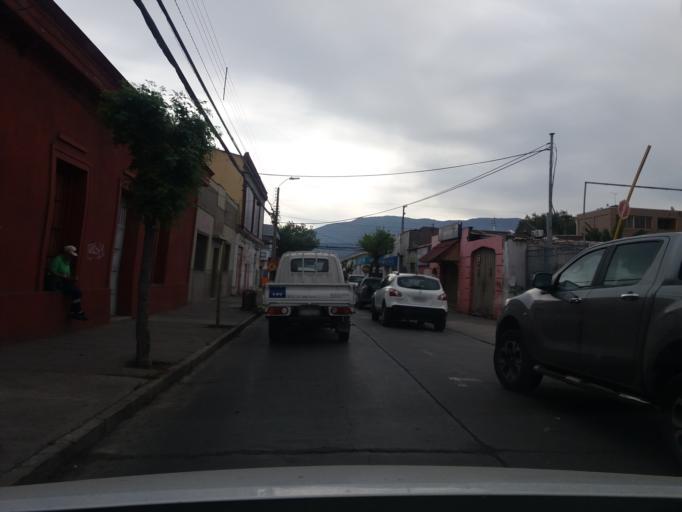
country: CL
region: Valparaiso
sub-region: Provincia de San Felipe
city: San Felipe
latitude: -32.7524
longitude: -70.7257
